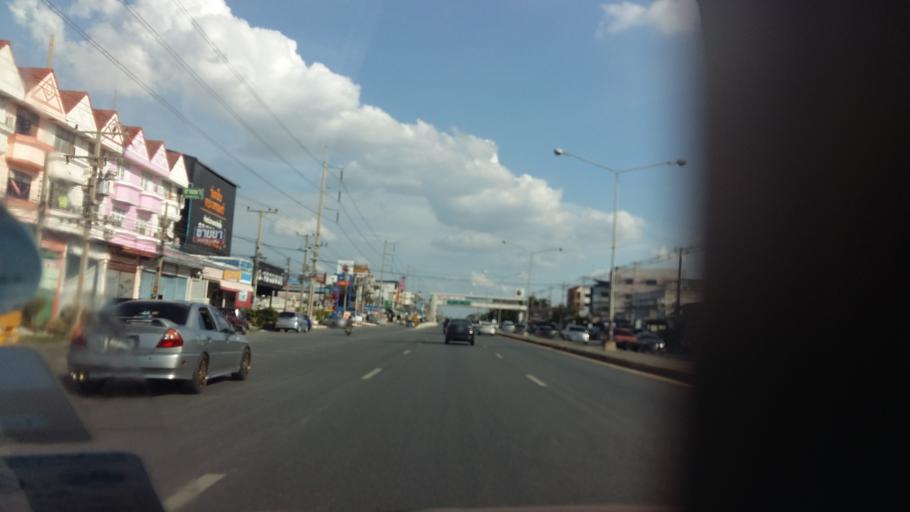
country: TH
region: Lop Buri
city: Lop Buri
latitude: 14.8291
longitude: 100.6466
